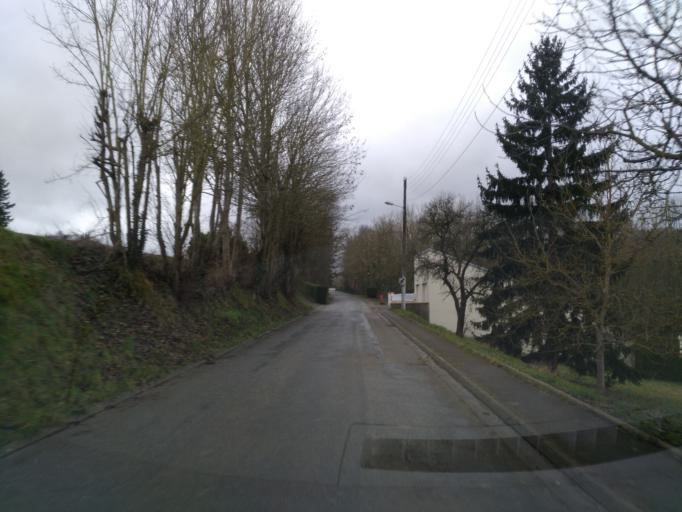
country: FR
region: Ile-de-France
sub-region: Departement des Yvelines
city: Mantes-la-Ville
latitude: 48.9502
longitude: 1.7063
